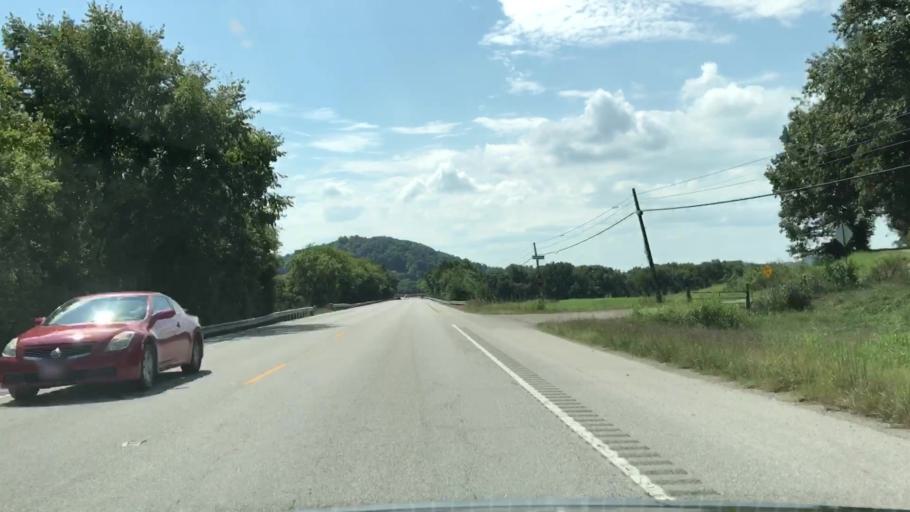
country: US
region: Tennessee
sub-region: Smith County
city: Carthage
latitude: 36.3118
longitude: -86.0088
